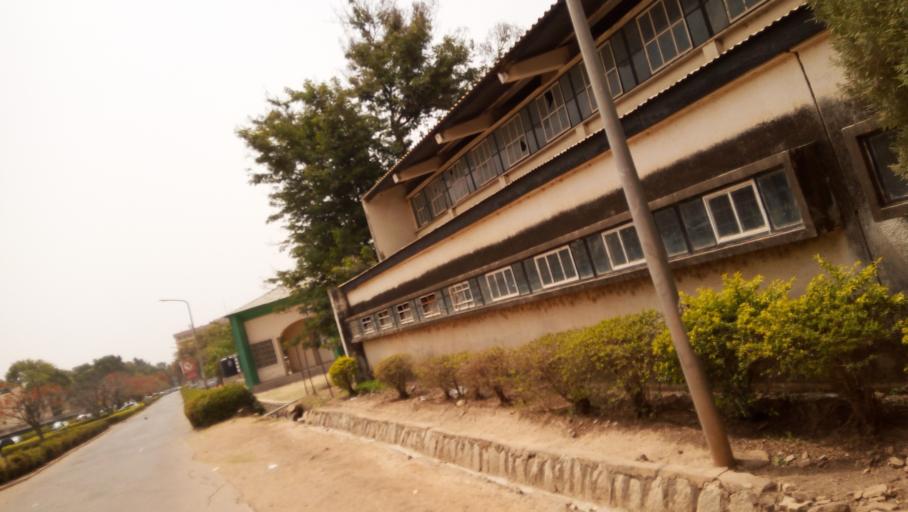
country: NG
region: Kaduna
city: Zaria
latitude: 11.1530
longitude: 7.6509
